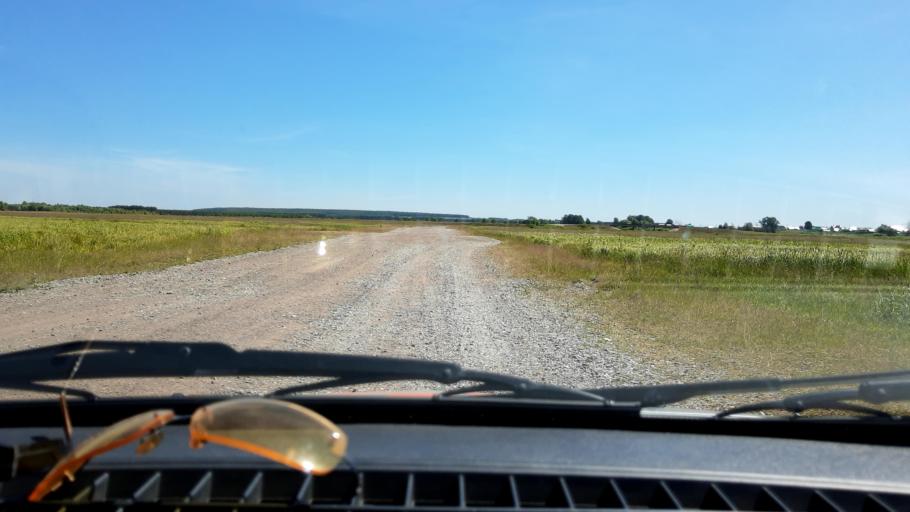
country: RU
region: Bashkortostan
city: Mikhaylovka
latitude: 54.9697
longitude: 55.7956
